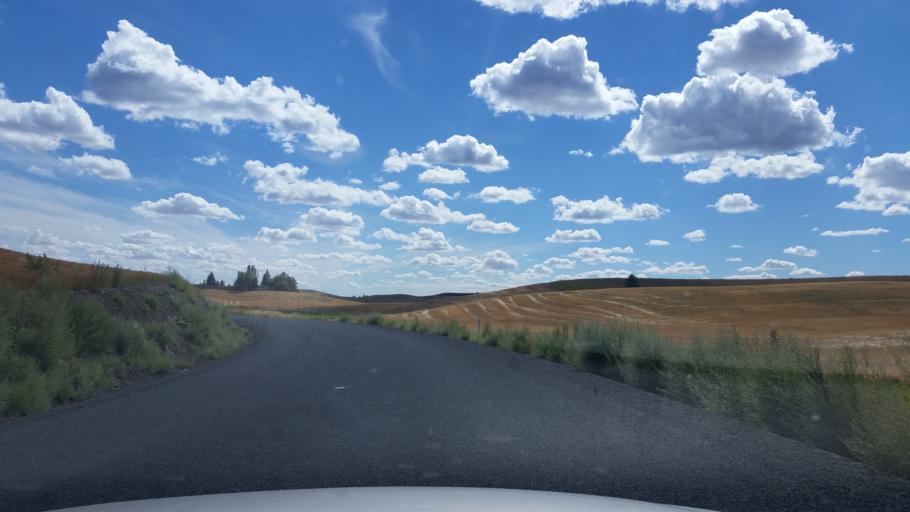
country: US
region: Washington
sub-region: Spokane County
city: Cheney
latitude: 47.4900
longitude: -117.6189
